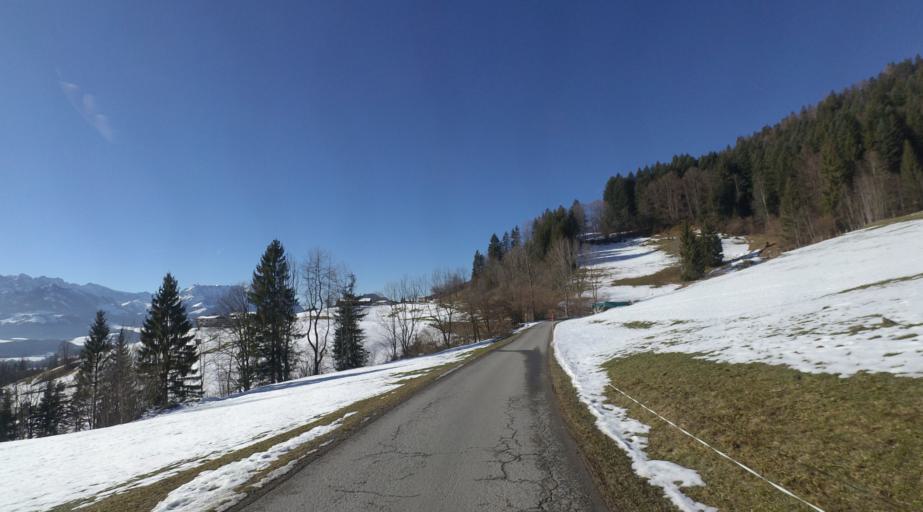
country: AT
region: Tyrol
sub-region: Politischer Bezirk Kitzbuhel
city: Kossen
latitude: 47.6820
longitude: 12.4275
